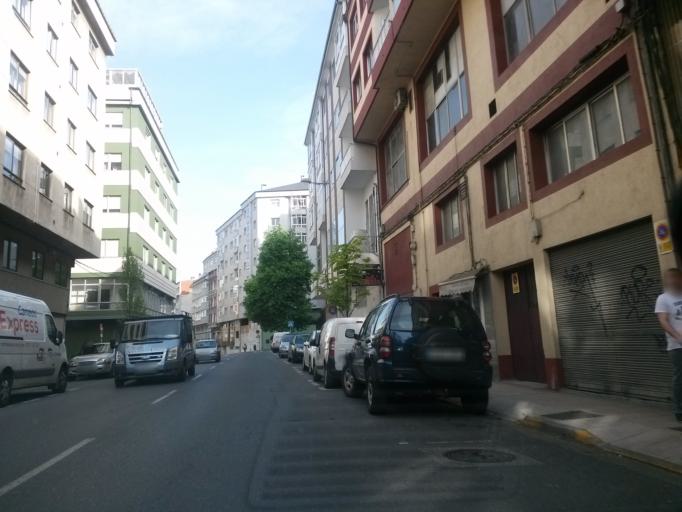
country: ES
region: Galicia
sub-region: Provincia de Lugo
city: Lugo
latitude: 43.0148
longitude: -7.5541
